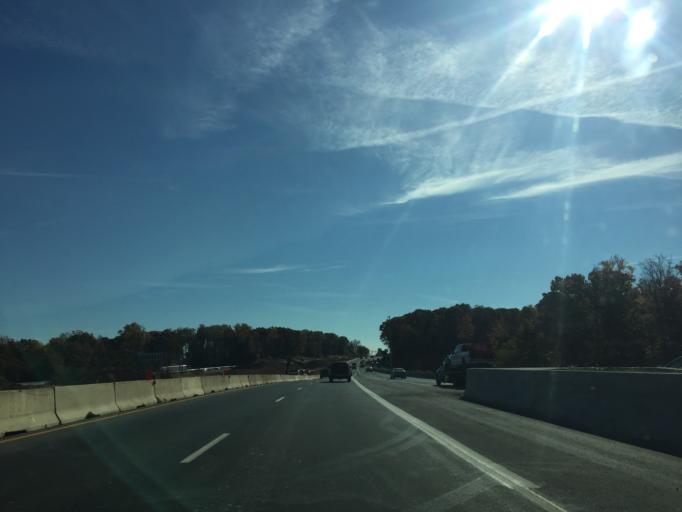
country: US
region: Maryland
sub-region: Baltimore County
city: Rossville
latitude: 39.3469
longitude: -76.4954
